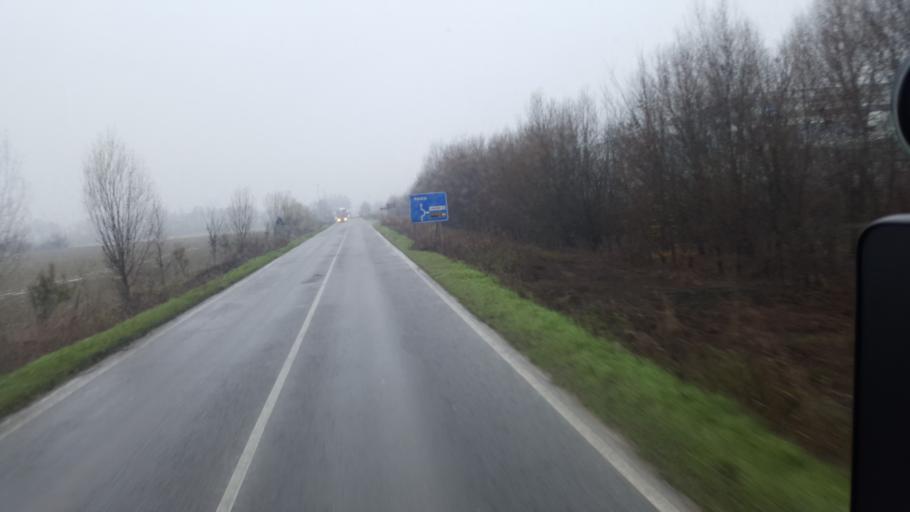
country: IT
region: Lombardy
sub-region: Provincia di Pavia
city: Landriano
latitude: 45.3012
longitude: 9.2575
